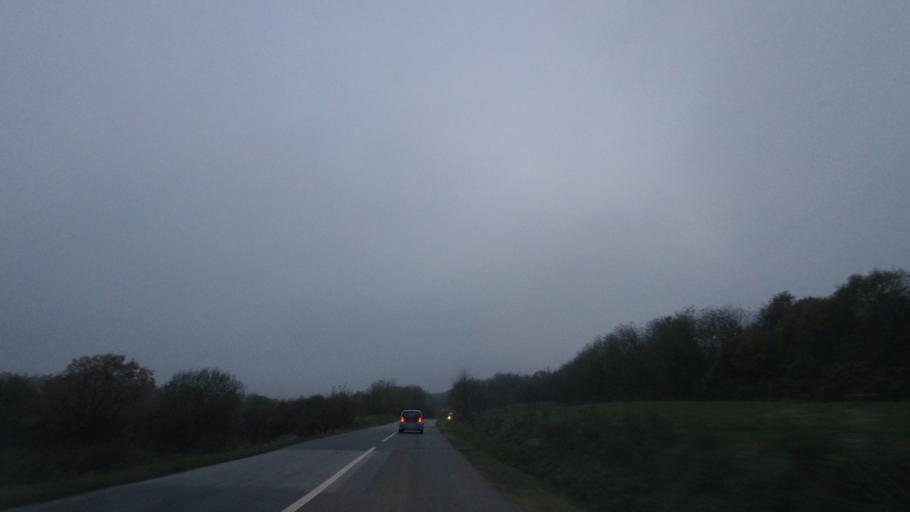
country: HR
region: Sisacko-Moslavacka
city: Glina
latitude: 45.4002
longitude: 16.1688
